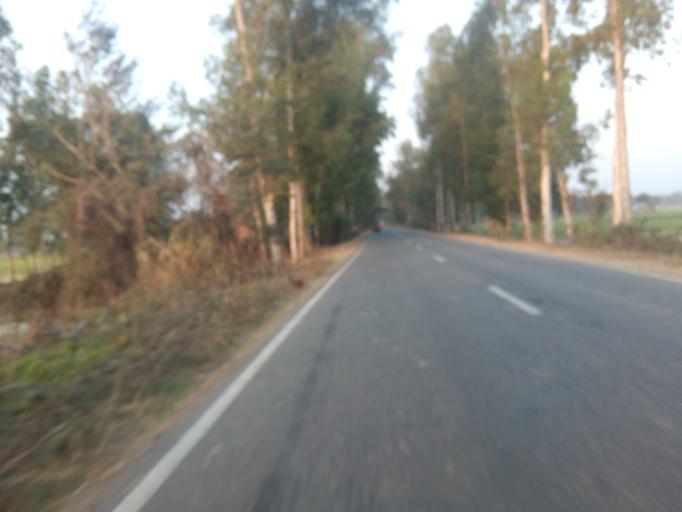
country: BD
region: Rajshahi
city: Bogra
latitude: 24.6298
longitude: 89.2452
